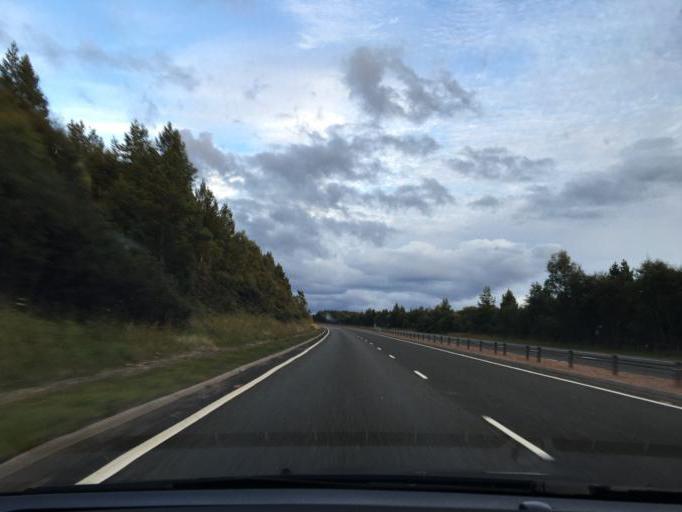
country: GB
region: Scotland
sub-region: Highland
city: Aviemore
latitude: 57.3188
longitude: -3.9699
